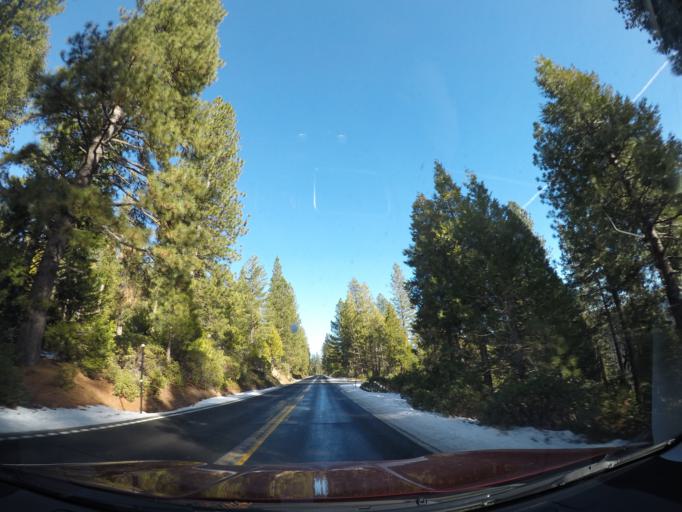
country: US
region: California
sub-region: Tuolumne County
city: Twain Harte
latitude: 38.1699
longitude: -120.0383
